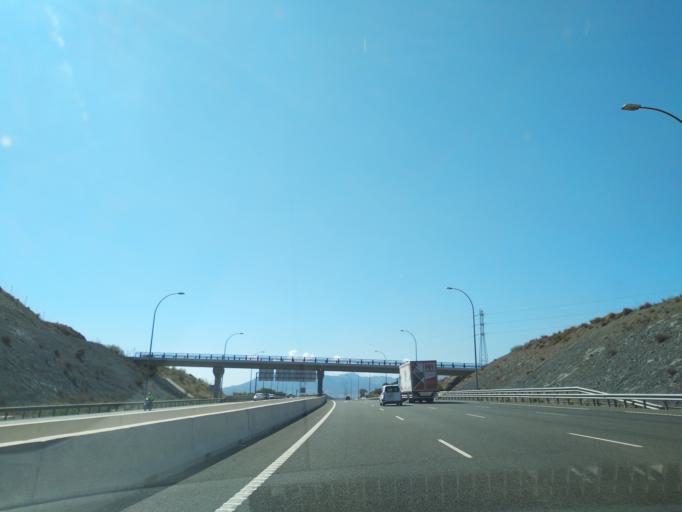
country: ES
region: Andalusia
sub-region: Provincia de Malaga
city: Malaga
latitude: 36.7438
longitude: -4.5020
